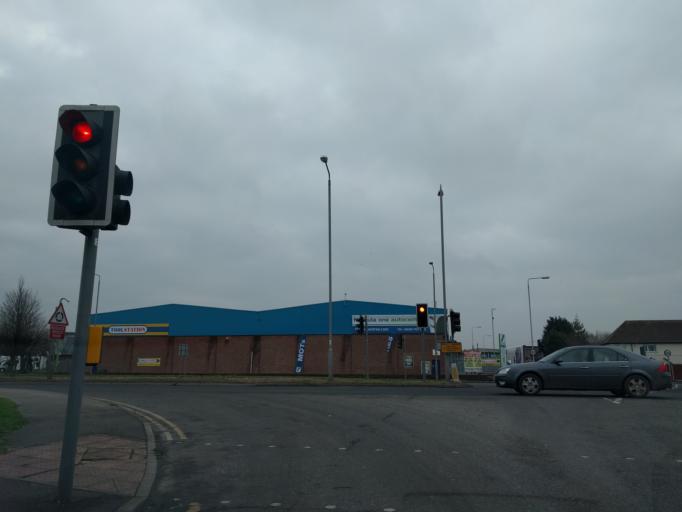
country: GB
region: England
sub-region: Nottinghamshire
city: Newark on Trent
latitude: 53.0918
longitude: -0.7901
